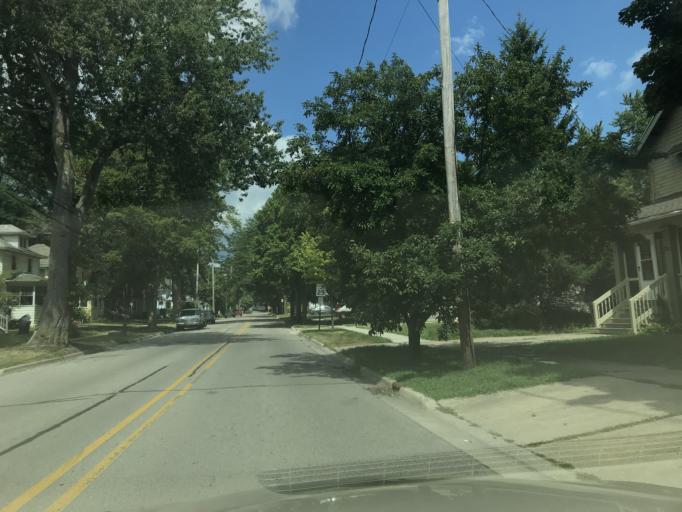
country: US
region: Michigan
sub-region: Jackson County
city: Jackson
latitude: 42.2415
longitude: -84.4185
